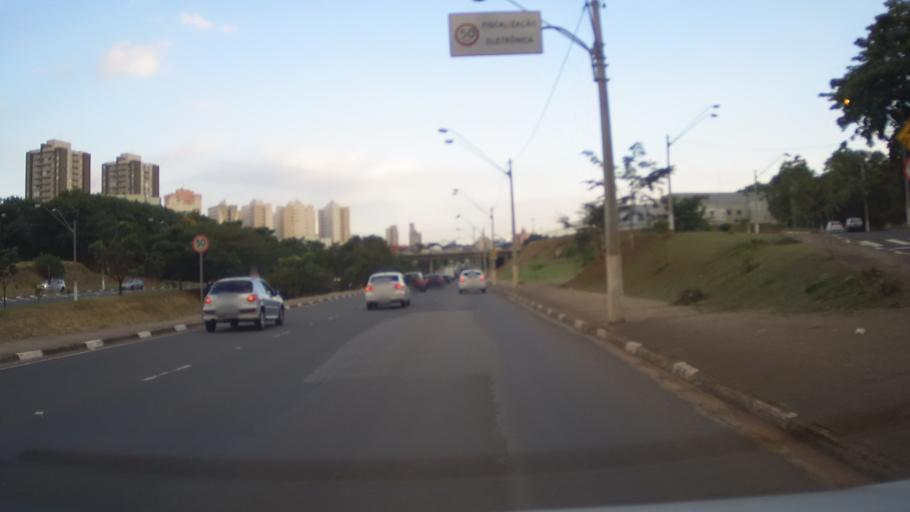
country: BR
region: Sao Paulo
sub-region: Campinas
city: Campinas
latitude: -22.9154
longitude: -47.0735
